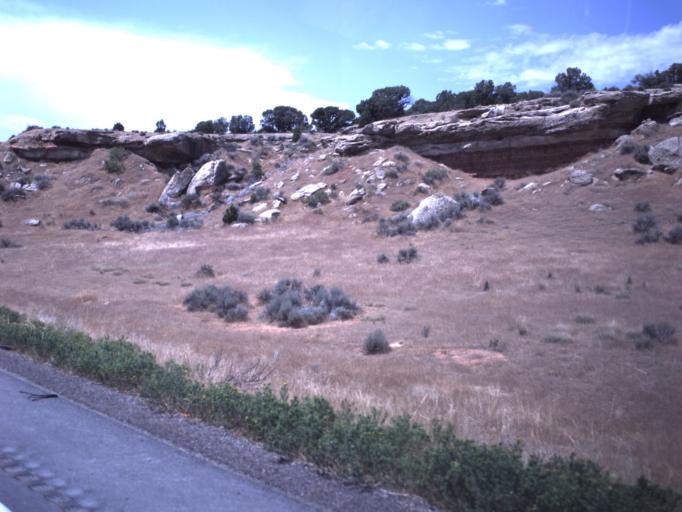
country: US
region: Utah
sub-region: Uintah County
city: Maeser
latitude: 40.3798
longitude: -109.6044
